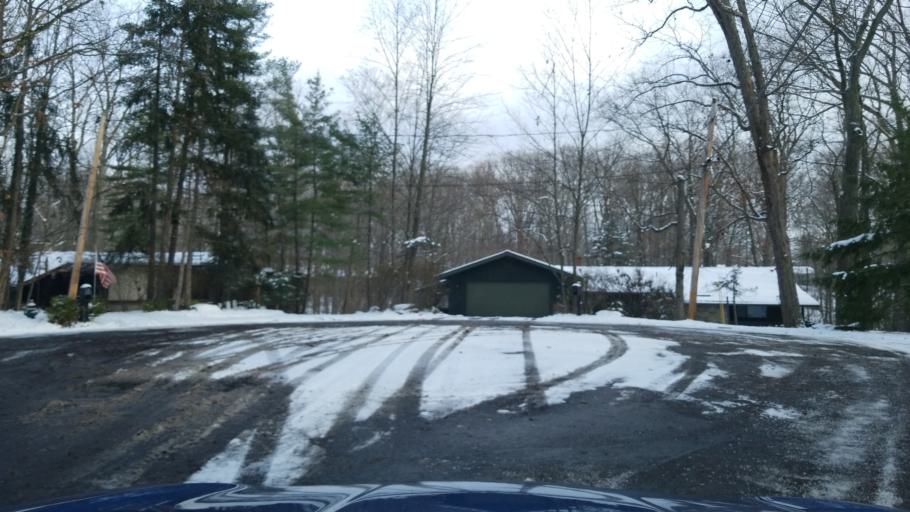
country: US
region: Ohio
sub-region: Cuyahoga County
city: Strongsville
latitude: 41.3346
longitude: -81.8416
